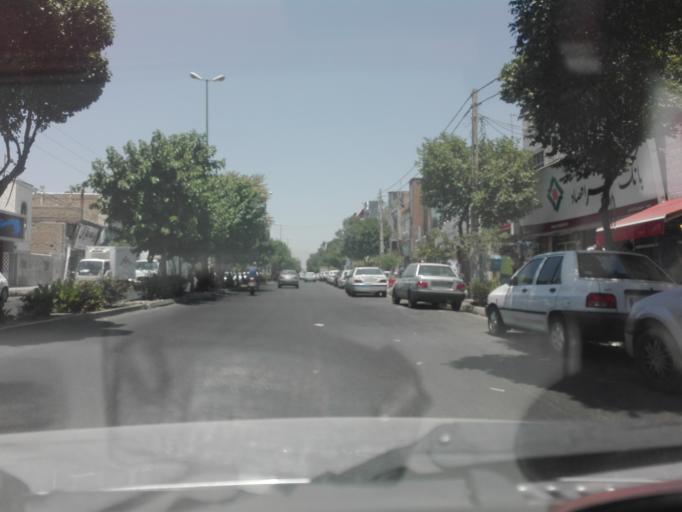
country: IR
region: Tehran
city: Malard
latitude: 35.7107
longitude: 50.9847
